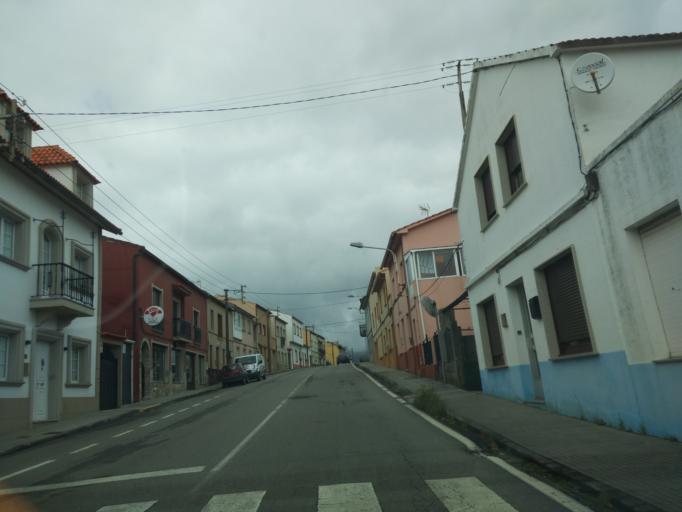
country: ES
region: Galicia
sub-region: Provincia da Coruna
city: Boiro
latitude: 42.6403
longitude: -8.8627
